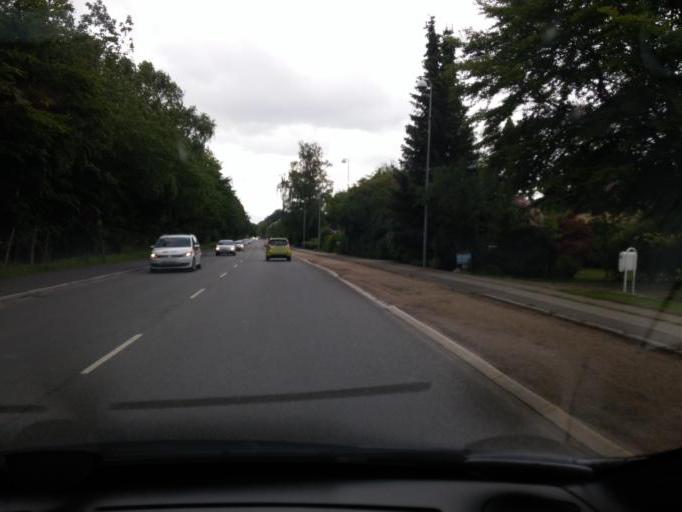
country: DK
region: Capital Region
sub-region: Hillerod Kommune
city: Hillerod
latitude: 55.9485
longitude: 12.3151
